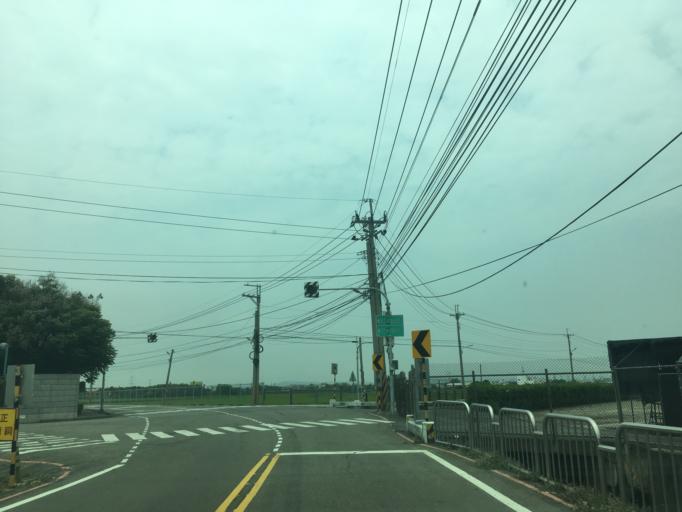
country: TW
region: Taiwan
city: Zhongxing New Village
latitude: 24.0291
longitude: 120.6890
